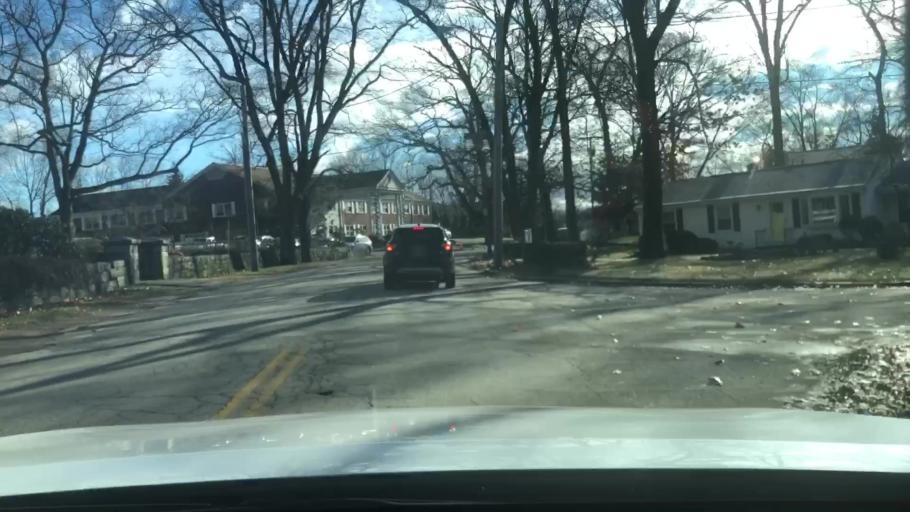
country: US
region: Rhode Island
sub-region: Providence County
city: Woonsocket
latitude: 42.0174
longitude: -71.4837
